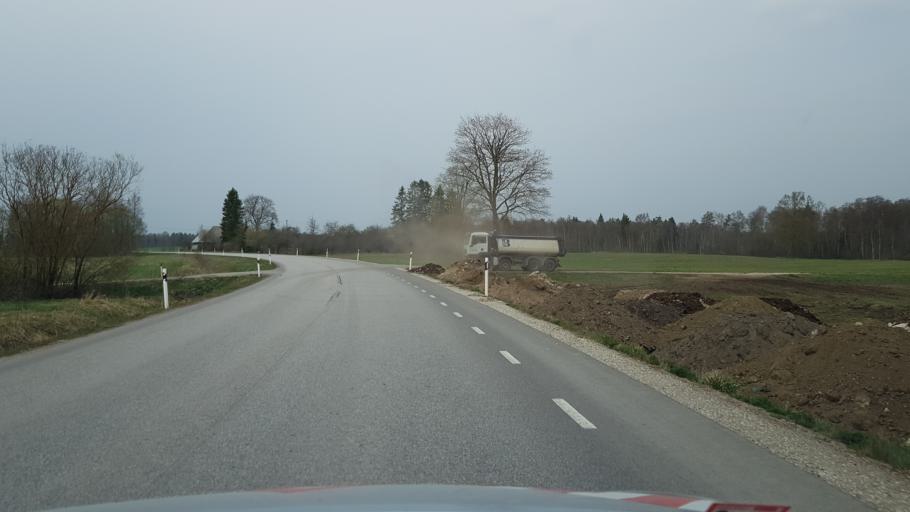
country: EE
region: Harju
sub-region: Raasiku vald
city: Arukula
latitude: 59.3713
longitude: 25.0266
